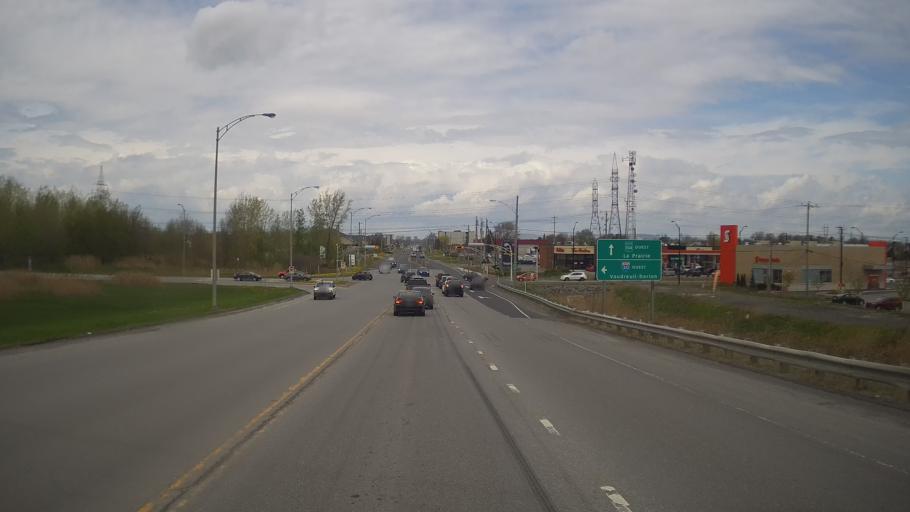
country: CA
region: Quebec
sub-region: Monteregie
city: La Prairie
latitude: 45.4042
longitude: -73.4624
